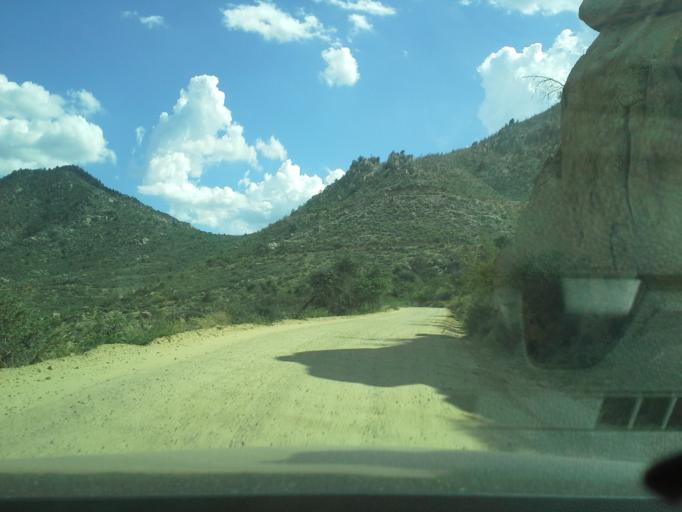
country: US
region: Arizona
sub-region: Yavapai County
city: Mayer
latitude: 34.2536
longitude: -112.2981
